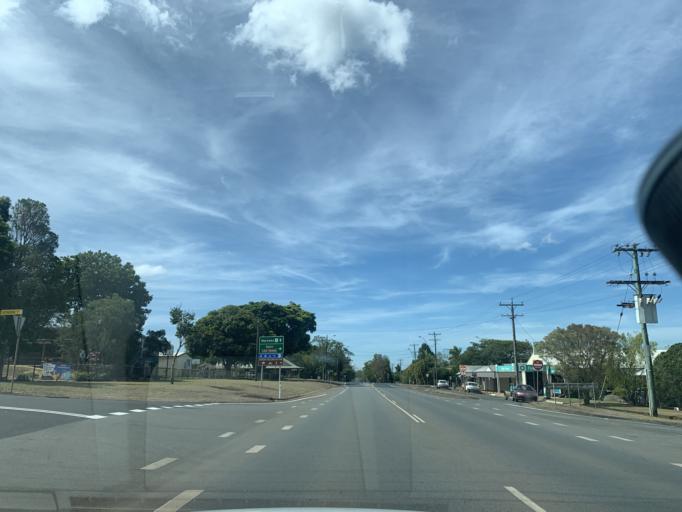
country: AU
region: Queensland
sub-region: Tablelands
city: Tolga
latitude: -17.2244
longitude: 145.4787
